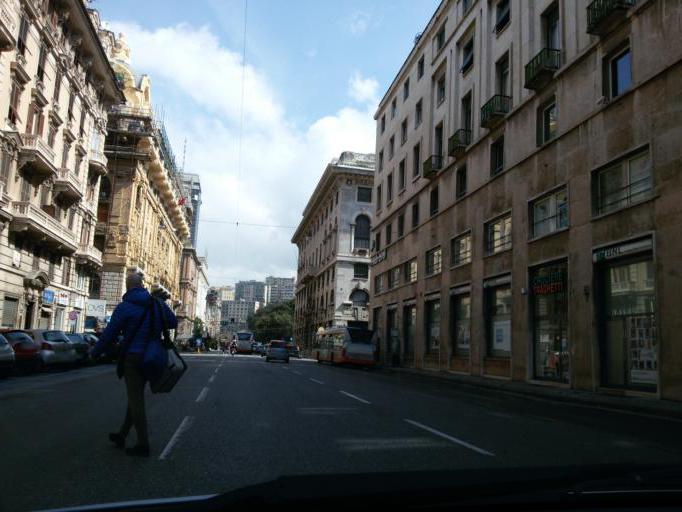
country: IT
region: Liguria
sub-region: Provincia di Genova
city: San Teodoro
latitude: 44.4036
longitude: 8.9437
